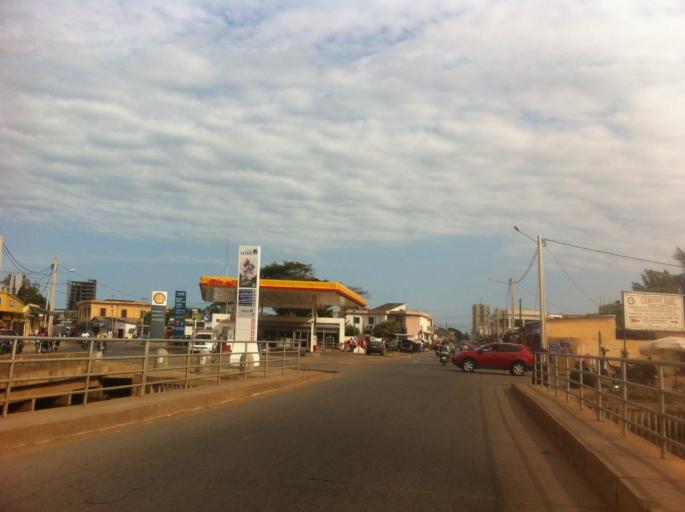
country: TG
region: Maritime
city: Lome
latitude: 6.1374
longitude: 1.2108
